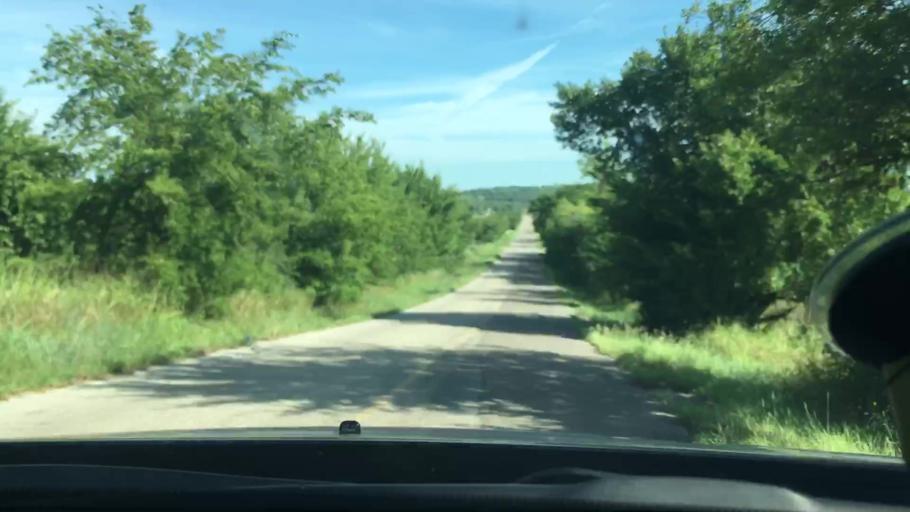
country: US
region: Oklahoma
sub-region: Carter County
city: Lone Grove
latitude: 34.3235
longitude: -97.2824
